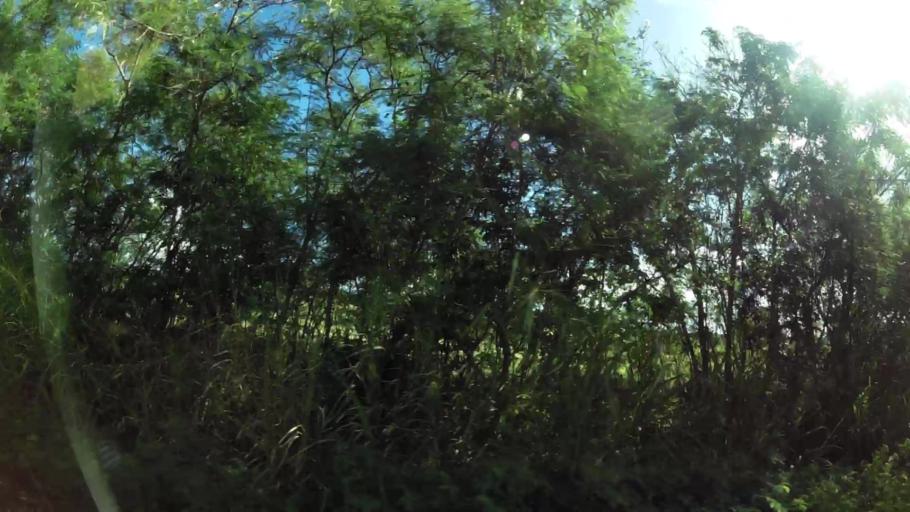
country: GP
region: Guadeloupe
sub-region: Guadeloupe
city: Petit-Canal
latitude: 16.3682
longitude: -61.4652
